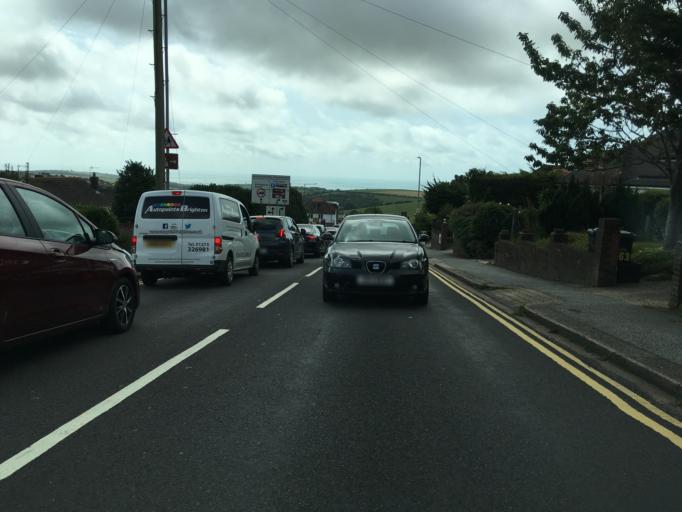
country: GB
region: England
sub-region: Brighton and Hove
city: Rottingdean
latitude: 50.8381
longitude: -0.0753
